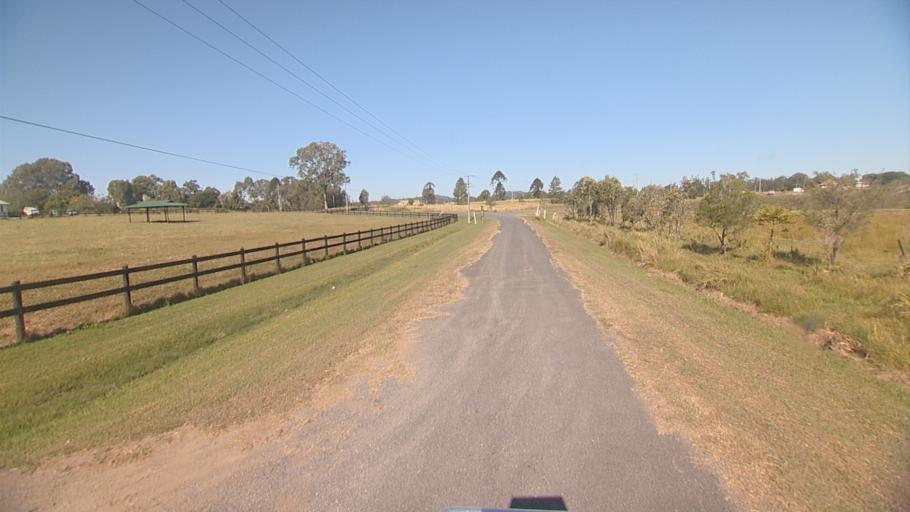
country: AU
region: Queensland
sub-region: Logan
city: Waterford West
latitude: -27.7066
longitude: 153.1314
